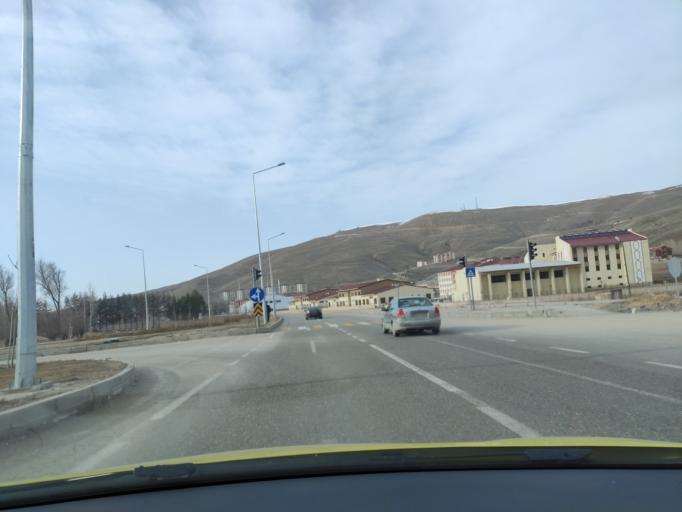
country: TR
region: Bayburt
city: Bayburt
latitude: 40.2317
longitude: 40.2566
